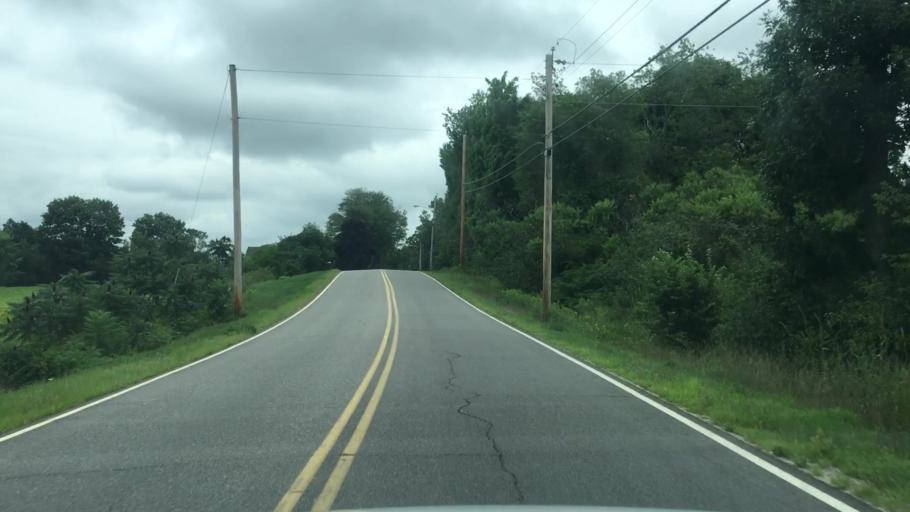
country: US
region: Maine
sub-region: York County
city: Dayton
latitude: 43.5300
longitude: -70.5176
